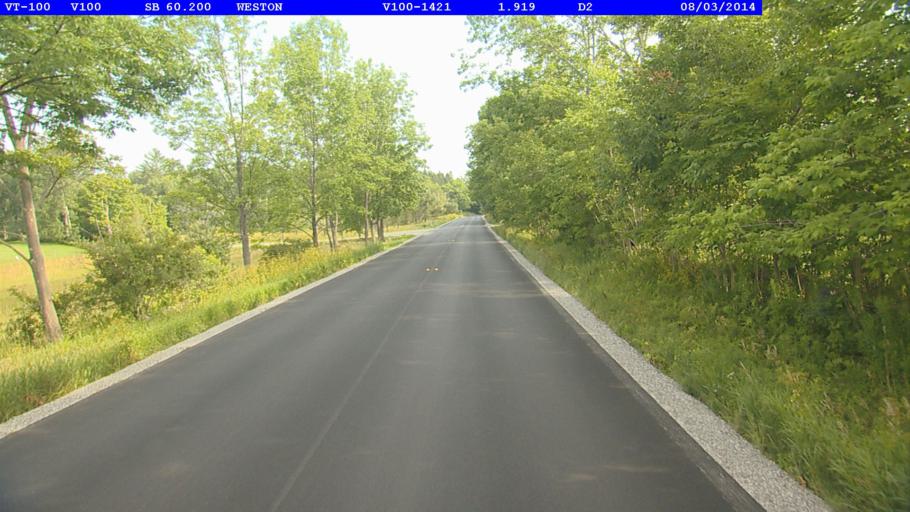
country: US
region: Vermont
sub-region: Windsor County
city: Chester
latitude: 43.2741
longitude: -72.7889
